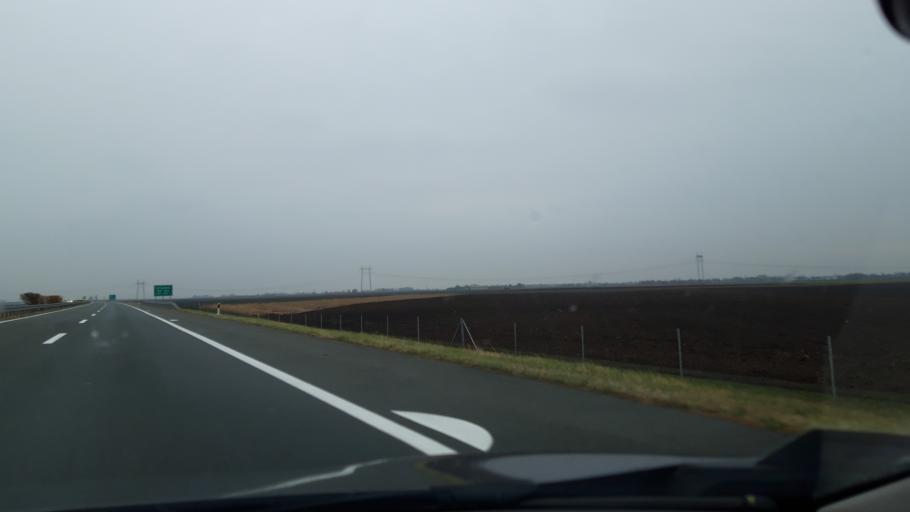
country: RS
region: Autonomna Pokrajina Vojvodina
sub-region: Severnobacki Okrug
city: Subotica
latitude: 46.0070
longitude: 19.7273
